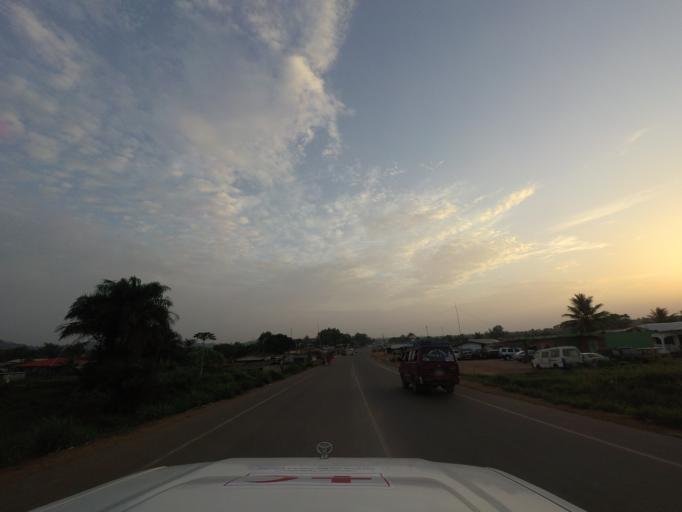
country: LR
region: Montserrado
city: Bensonville City
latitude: 6.3236
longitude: -10.6633
